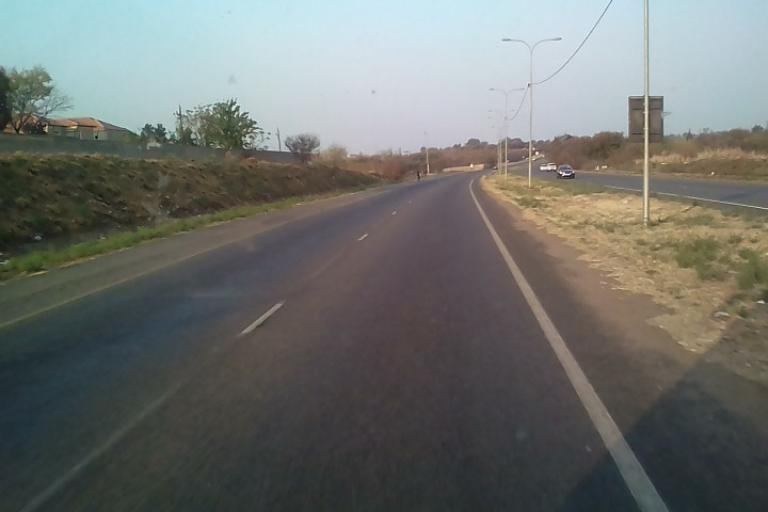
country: ZA
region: Gauteng
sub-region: City of Johannesburg Metropolitan Municipality
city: Johannesburg
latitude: -26.3141
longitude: 28.0667
